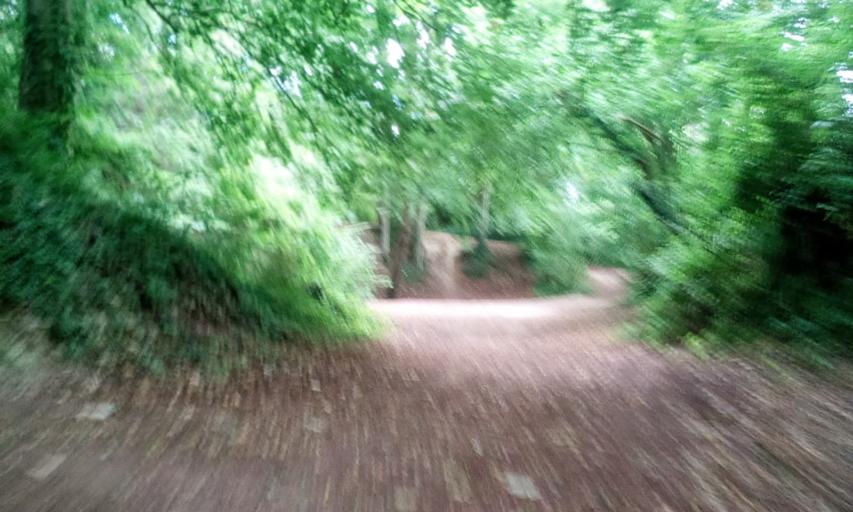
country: FR
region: Lower Normandy
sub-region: Departement du Calvados
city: Bellengreville
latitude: 49.1157
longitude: -0.2021
